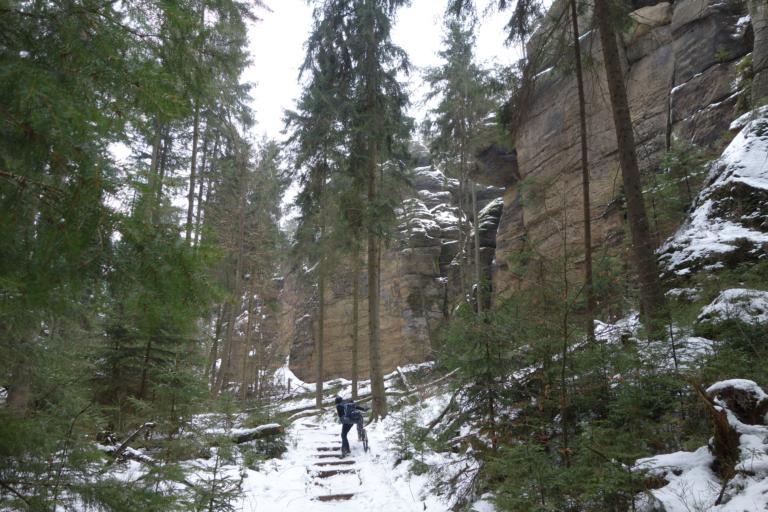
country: DE
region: Saxony
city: Bad Schandau
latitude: 50.9172
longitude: 14.1924
